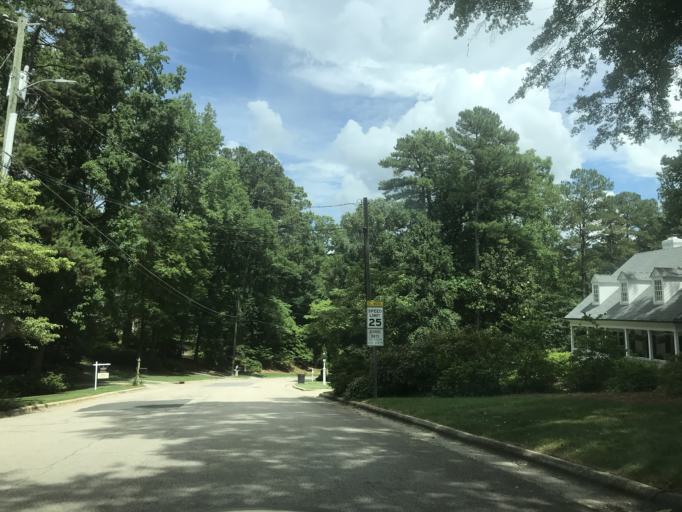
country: US
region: North Carolina
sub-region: Wake County
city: West Raleigh
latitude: 35.8291
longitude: -78.6468
